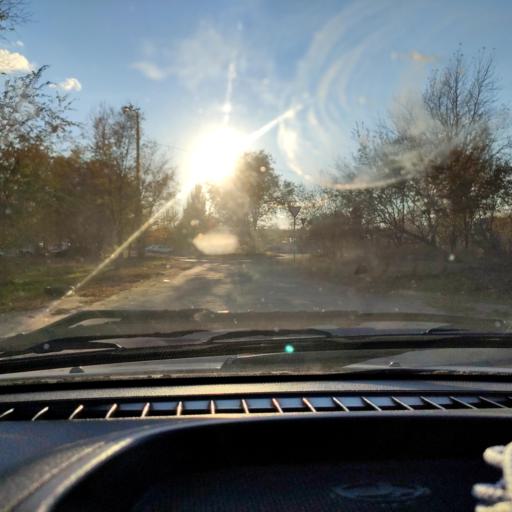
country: RU
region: Samara
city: Zhigulevsk
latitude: 53.4856
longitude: 49.5193
